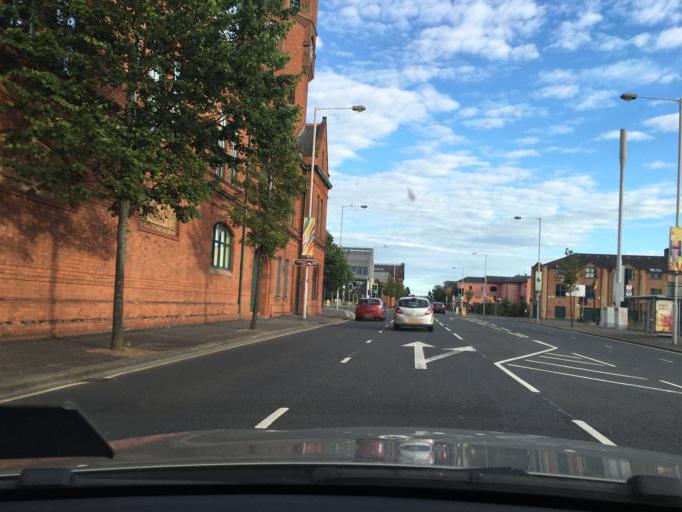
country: GB
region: Northern Ireland
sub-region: City of Belfast
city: Belfast
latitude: 54.5913
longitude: -5.9256
